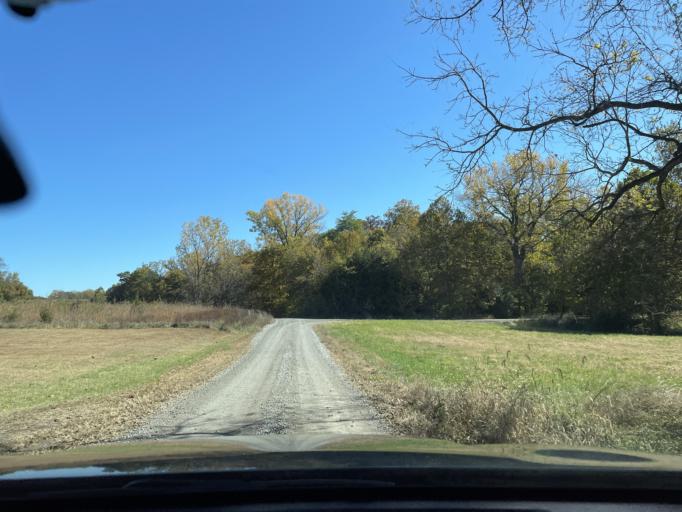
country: US
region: Missouri
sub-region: Andrew County
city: Savannah
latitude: 39.9373
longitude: -94.8650
